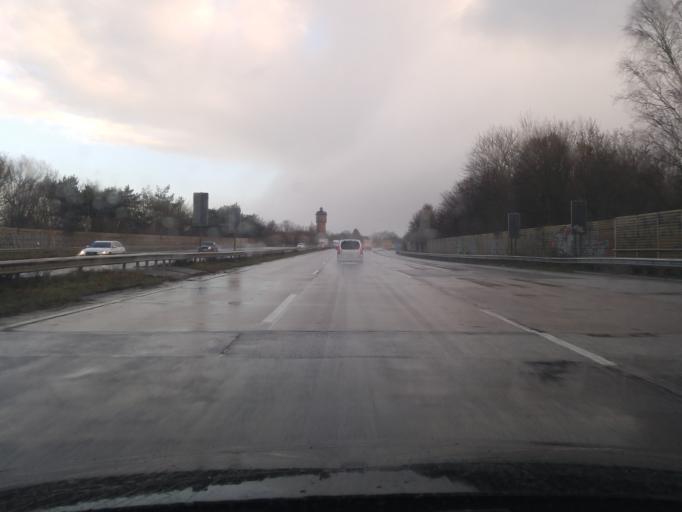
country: DE
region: Schleswig-Holstein
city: Bad Schwartau
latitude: 53.9030
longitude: 10.6837
